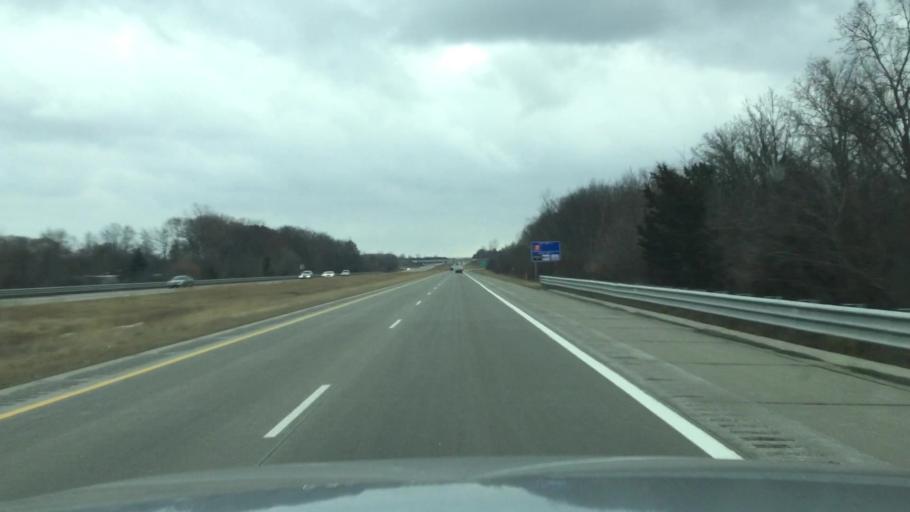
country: US
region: Michigan
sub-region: Genesee County
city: Flint
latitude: 42.9549
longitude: -83.6825
